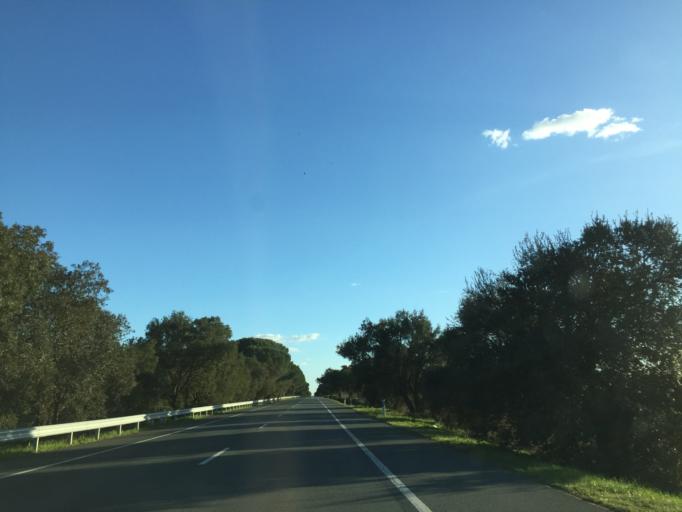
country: PT
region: Beja
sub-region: Aljustrel
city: Aljustrel
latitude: 37.9786
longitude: -8.3826
